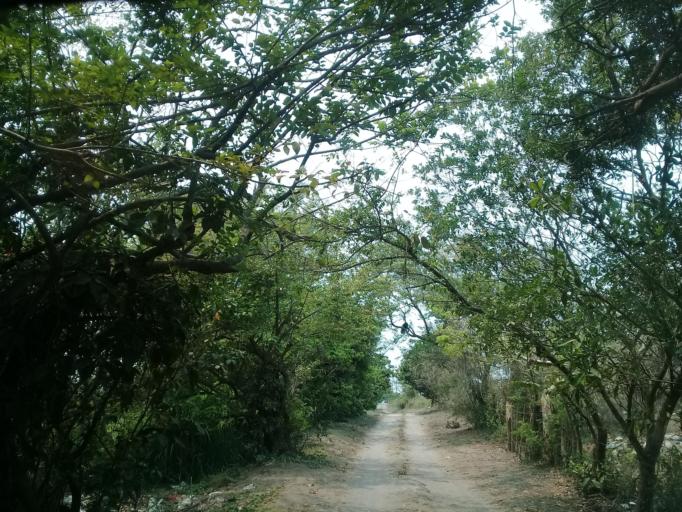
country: MX
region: Veracruz
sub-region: Veracruz
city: Hacienda Sotavento
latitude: 19.1399
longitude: -96.1587
